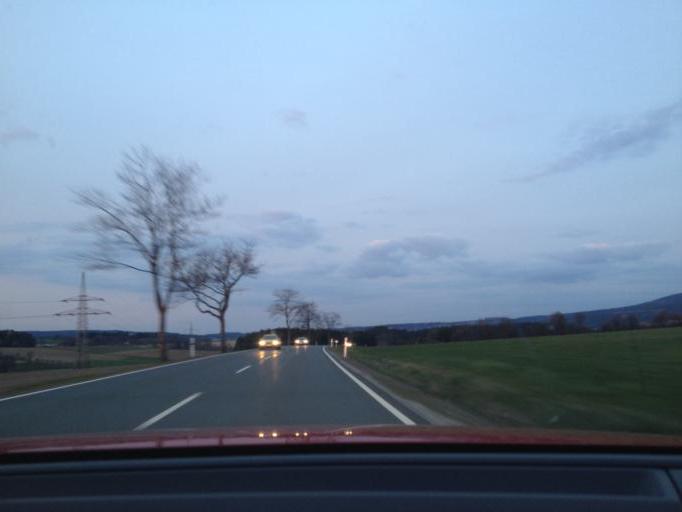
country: DE
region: Bavaria
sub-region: Upper Palatinate
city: Neusorg
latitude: 49.9068
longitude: 11.9384
